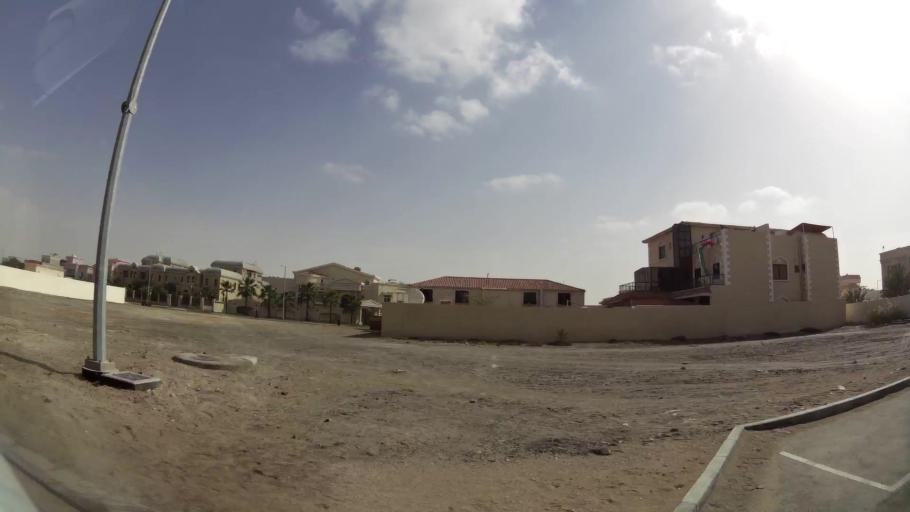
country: AE
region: Abu Dhabi
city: Abu Dhabi
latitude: 24.4251
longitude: 54.5598
